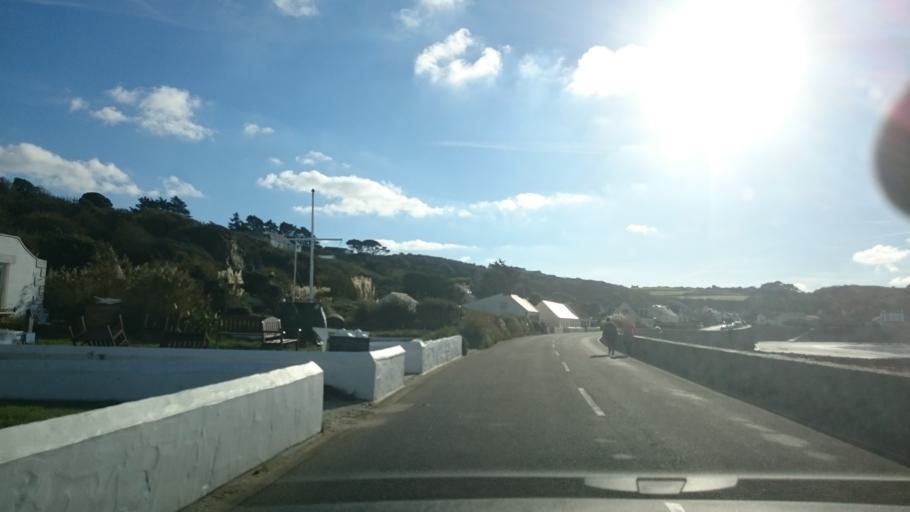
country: GG
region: St Peter Port
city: Saint Peter Port
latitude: 49.4371
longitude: -2.6537
